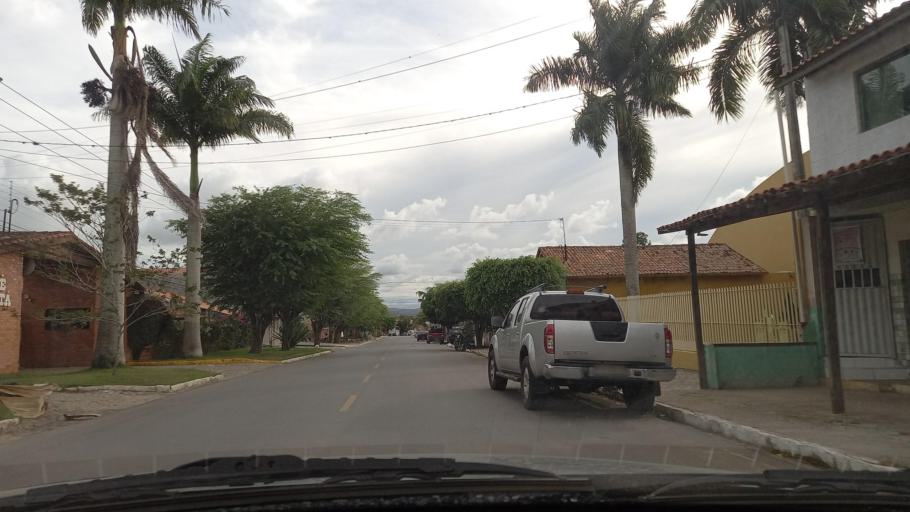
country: BR
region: Pernambuco
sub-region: Gravata
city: Gravata
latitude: -8.1938
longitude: -35.5463
